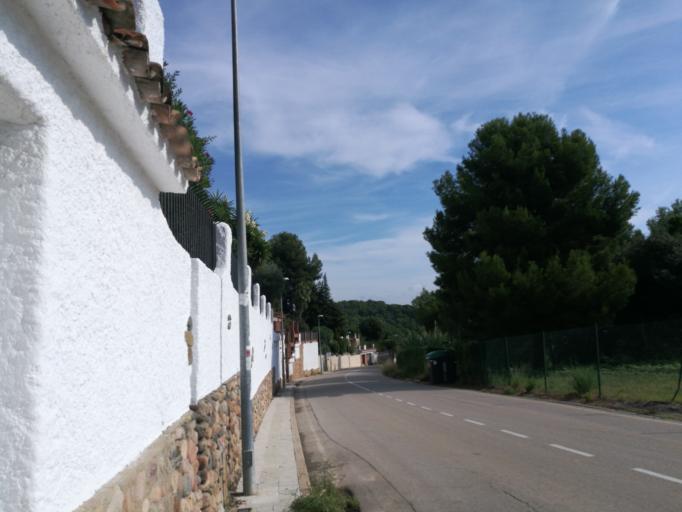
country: ES
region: Catalonia
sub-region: Provincia de Girona
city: Blanes
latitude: 41.6869
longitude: 2.8116
